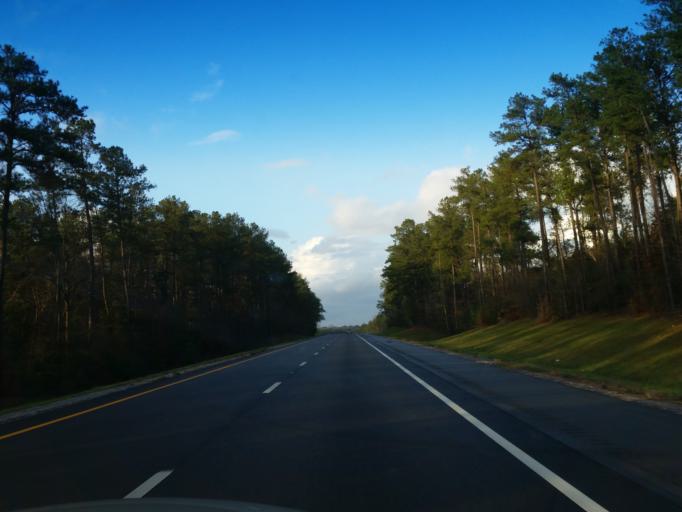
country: US
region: Mississippi
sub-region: Jones County
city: Sharon
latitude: 31.8579
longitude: -89.0471
